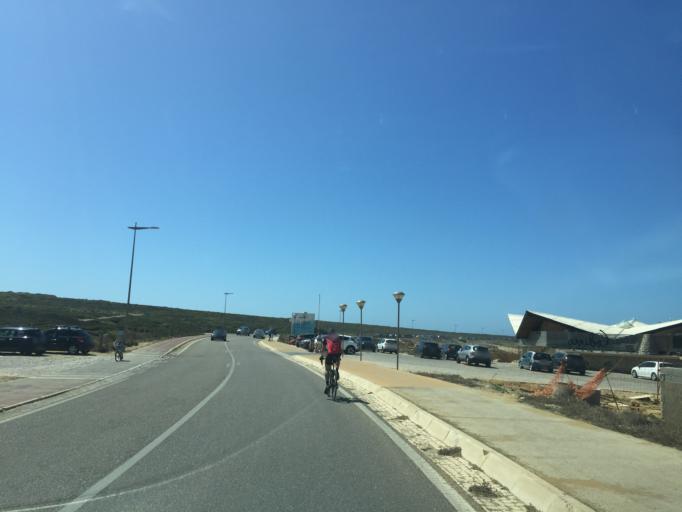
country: PT
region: Lisbon
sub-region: Cascais
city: Cascais
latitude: 38.7223
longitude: -9.4779
